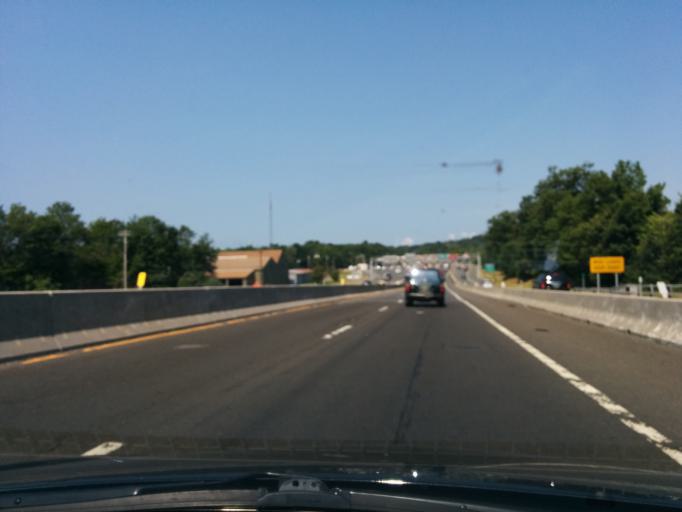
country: US
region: New York
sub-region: Orange County
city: Central Valley
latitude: 41.3119
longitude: -74.1238
